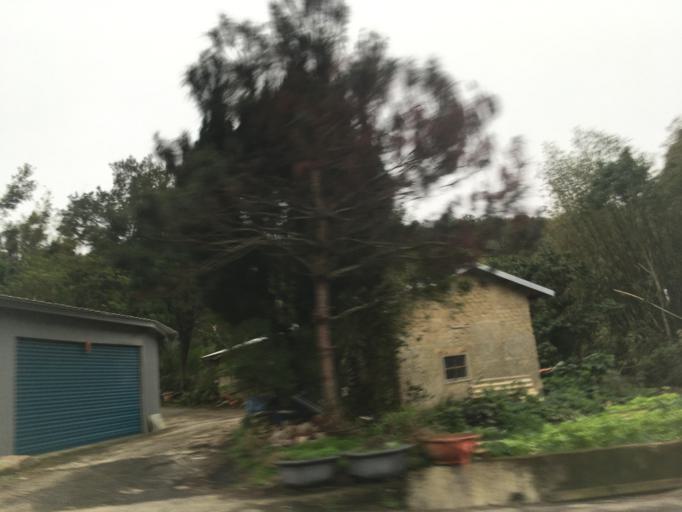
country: TW
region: Taiwan
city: Fengyuan
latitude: 24.4114
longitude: 120.7379
